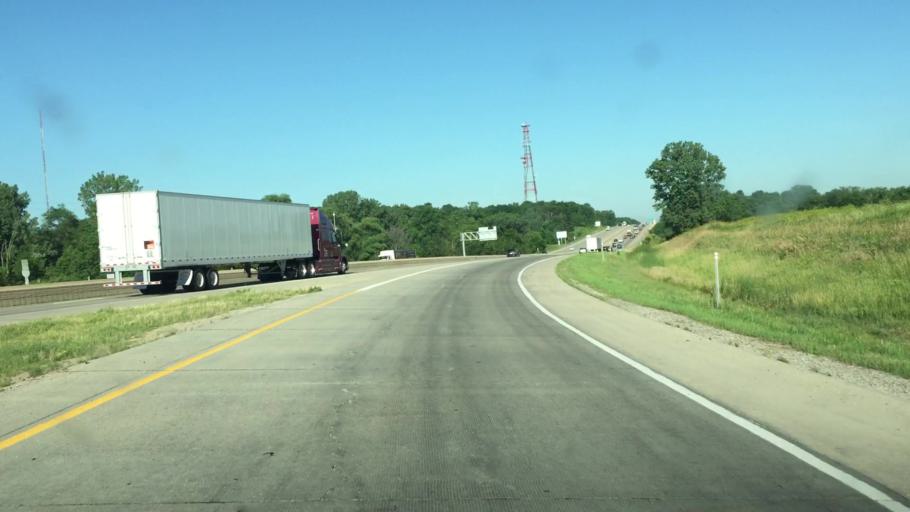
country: US
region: Iowa
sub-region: Johnson County
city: Iowa City
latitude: 41.6871
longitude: -91.5026
